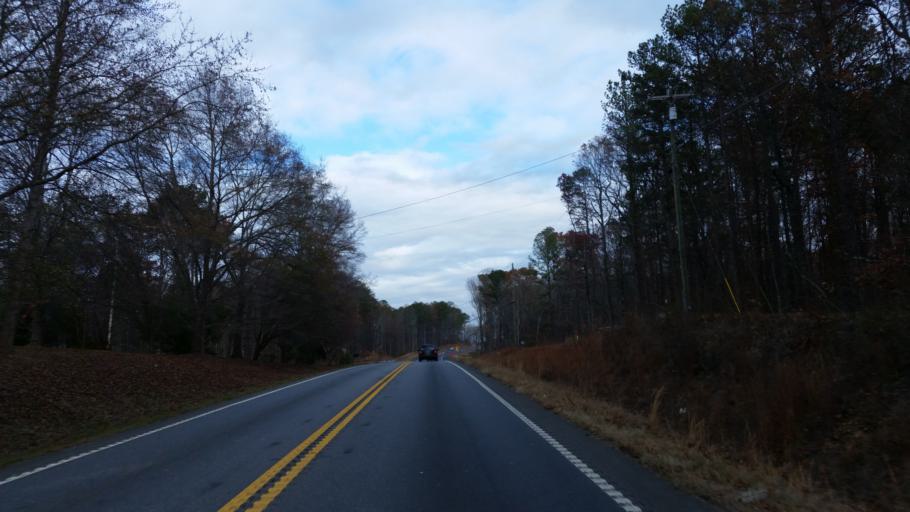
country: US
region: Georgia
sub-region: Cherokee County
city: Holly Springs
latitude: 34.2217
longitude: -84.6241
